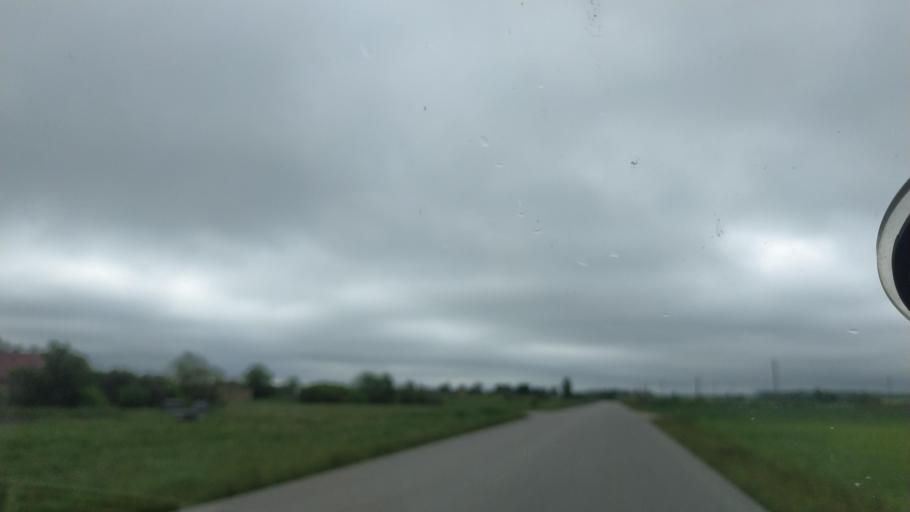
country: LT
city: Vabalninkas
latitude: 55.9731
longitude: 24.7425
